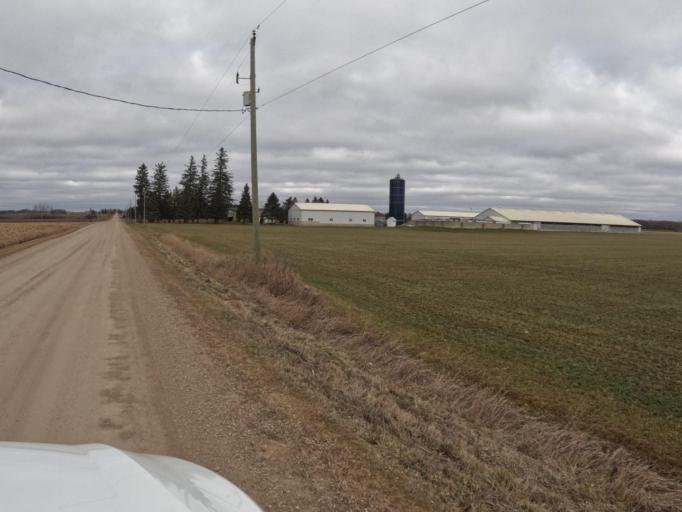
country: CA
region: Ontario
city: Shelburne
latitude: 43.8629
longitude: -80.4002
